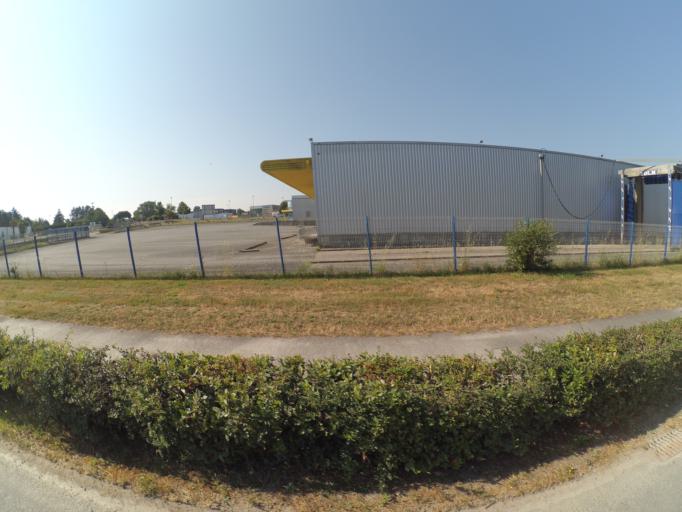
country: FR
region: Pays de la Loire
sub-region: Departement de la Vendee
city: Treize-Septiers
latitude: 46.9864
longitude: -1.2204
